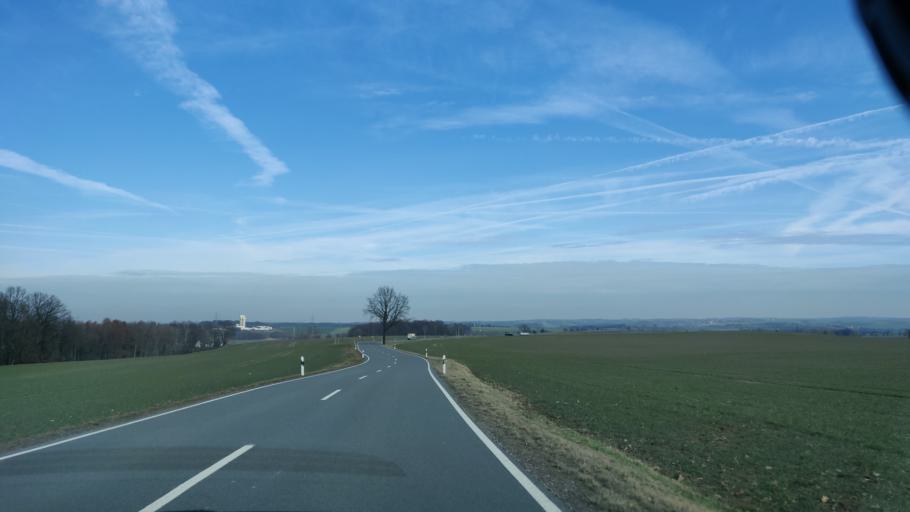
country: DE
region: Saxony
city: Konigsfeld
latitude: 51.0814
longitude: 12.7284
